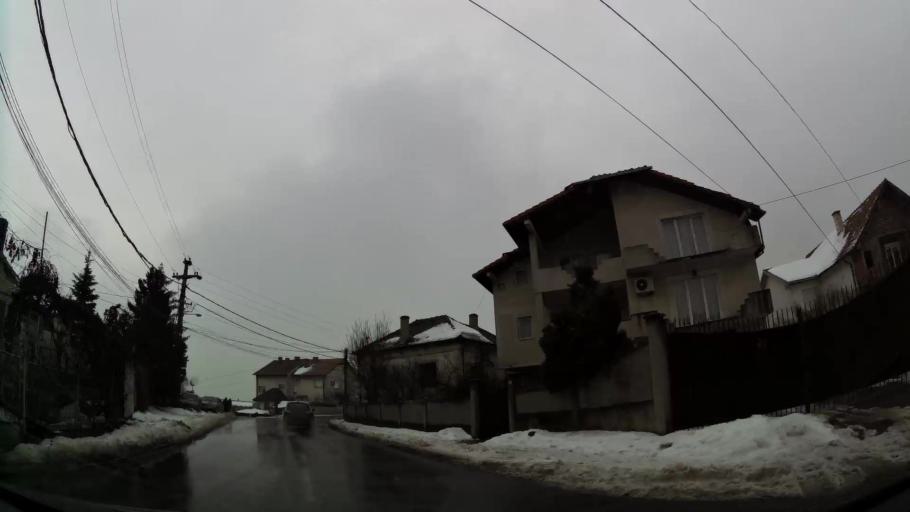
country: RS
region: Central Serbia
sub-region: Belgrade
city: Zvezdara
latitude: 44.7718
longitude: 20.5354
